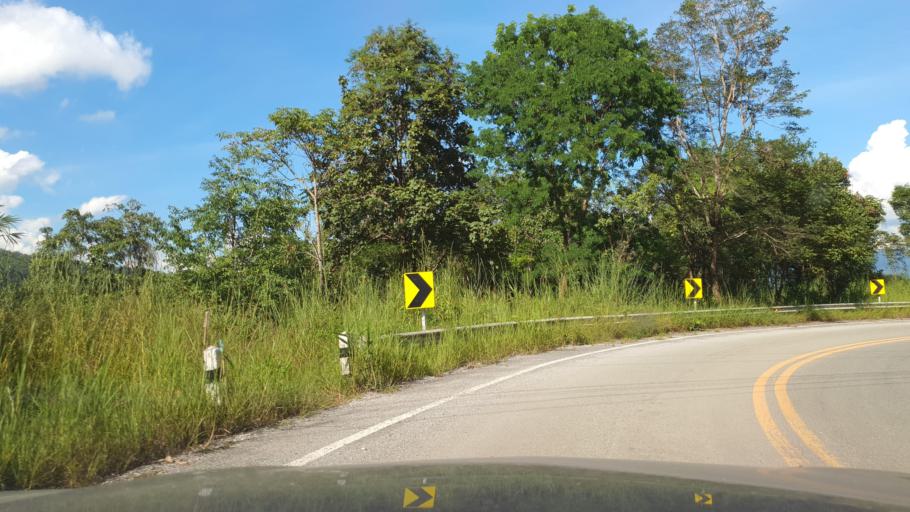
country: TH
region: Chiang Rai
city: Wiang Pa Pao
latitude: 19.3286
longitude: 99.4457
